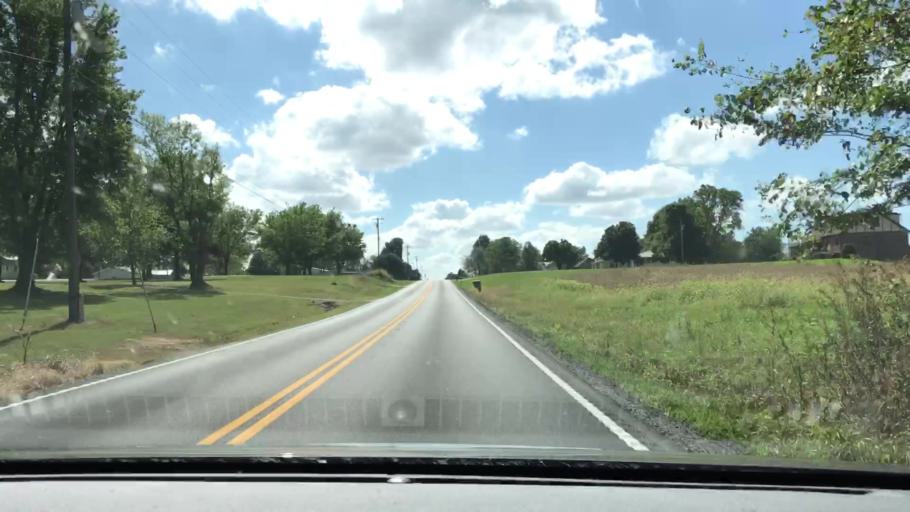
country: US
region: Kentucky
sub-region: Graves County
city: Mayfield
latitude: 36.8055
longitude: -88.5953
